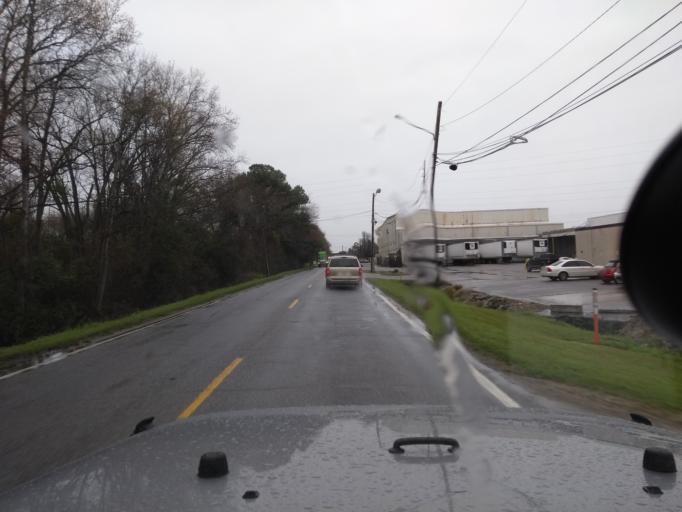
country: US
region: Georgia
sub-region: Chatham County
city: Garden City
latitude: 32.0855
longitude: -81.1365
